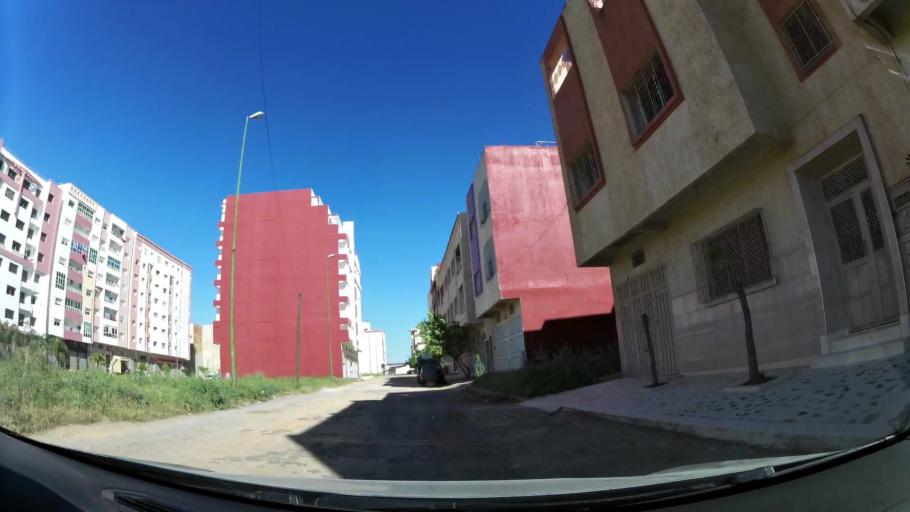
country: MA
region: Meknes-Tafilalet
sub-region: Meknes
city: Meknes
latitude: 33.8796
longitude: -5.5798
